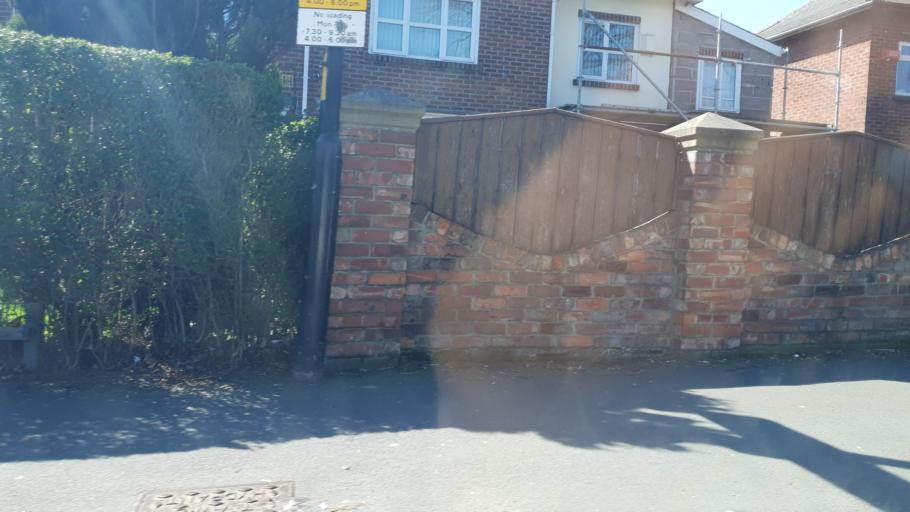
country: GB
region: England
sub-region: Middlesbrough
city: Middlesbrough
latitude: 54.5558
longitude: -1.2219
